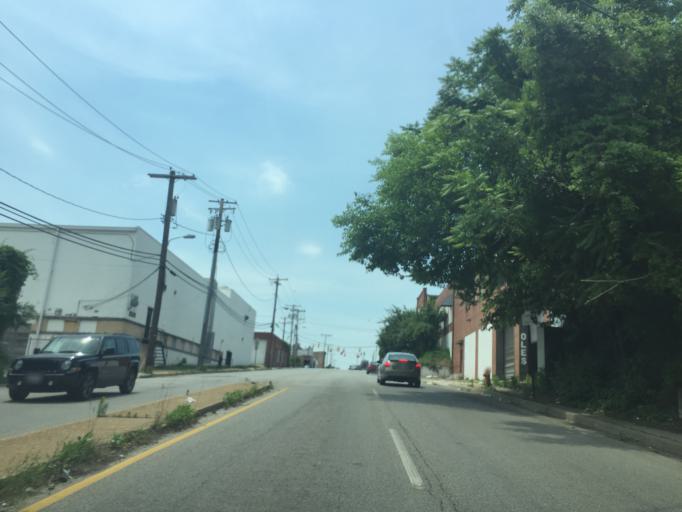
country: US
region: Maryland
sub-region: City of Baltimore
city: Baltimore
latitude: 39.3195
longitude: -76.6058
